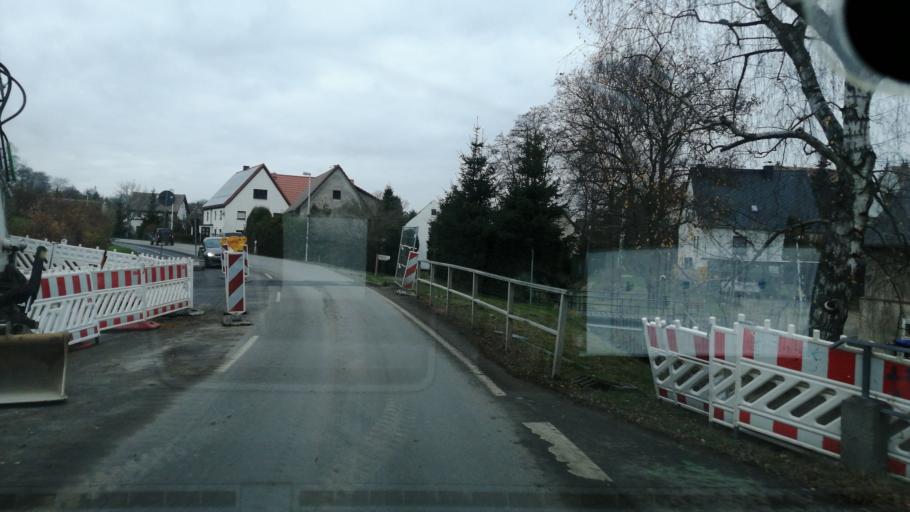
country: DE
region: Saxony
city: Bernstadt
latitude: 51.0679
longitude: 14.7934
